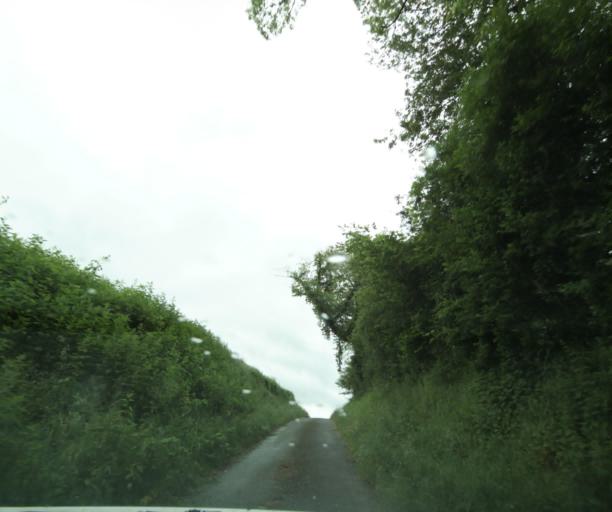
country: FR
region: Bourgogne
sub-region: Departement de Saone-et-Loire
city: Palinges
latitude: 46.4916
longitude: 4.2454
